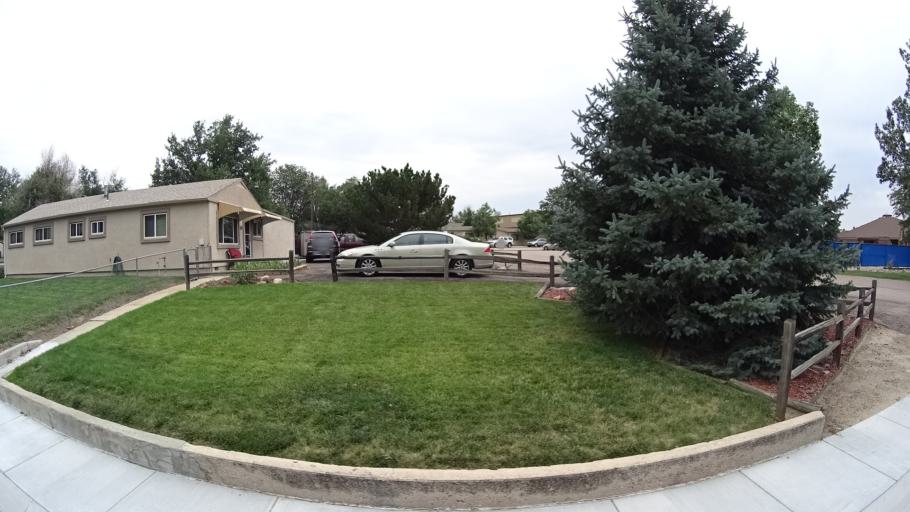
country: US
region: Colorado
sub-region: El Paso County
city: Colorado Springs
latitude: 38.8926
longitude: -104.8148
